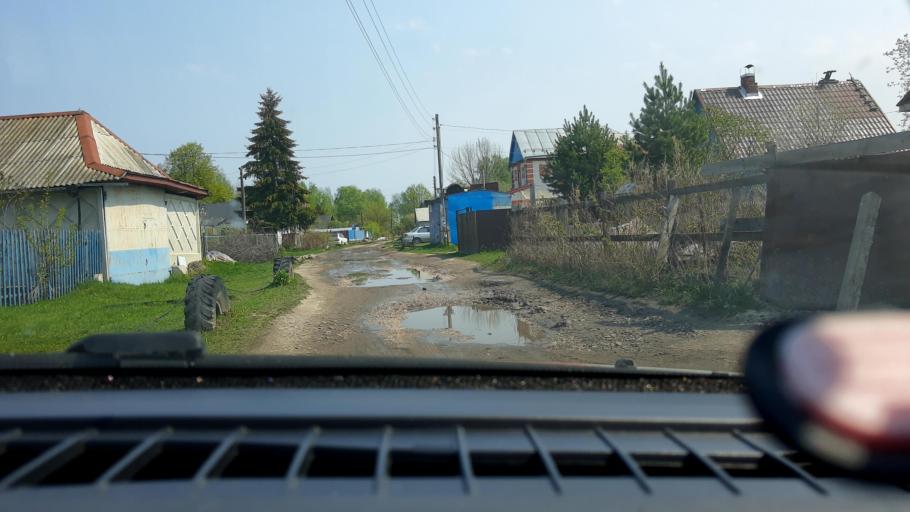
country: RU
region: Nizjnij Novgorod
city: Gorbatovka
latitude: 56.2684
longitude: 43.7918
